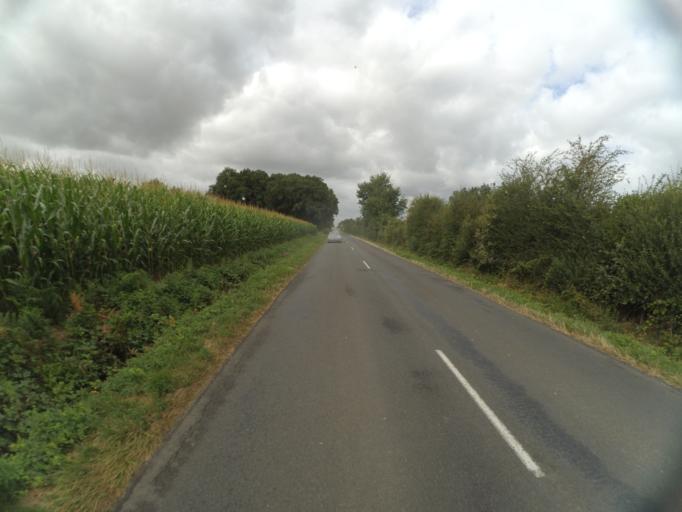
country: FR
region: Pays de la Loire
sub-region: Departement de Maine-et-Loire
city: Villedieu-la-Blouere
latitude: 47.1349
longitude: -1.0790
